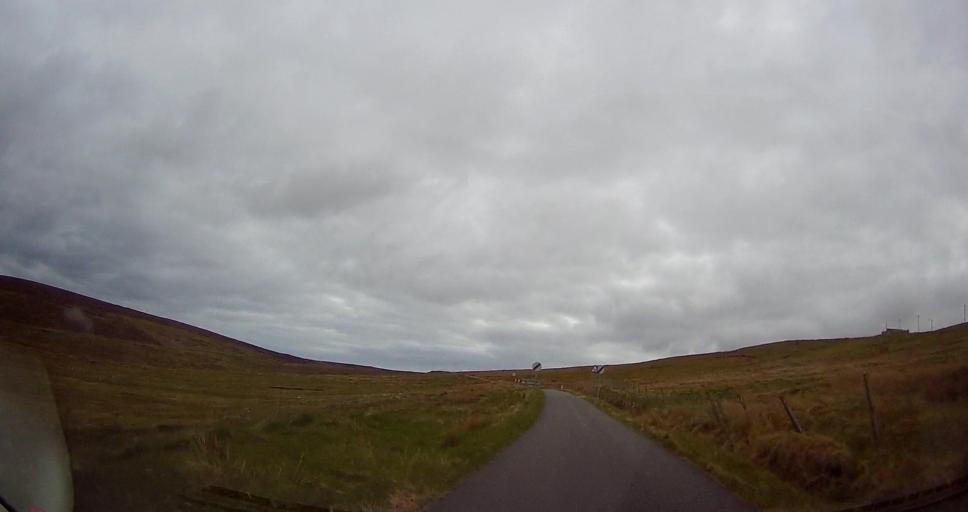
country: GB
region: Scotland
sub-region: Shetland Islands
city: Shetland
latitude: 60.5953
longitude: -1.0740
